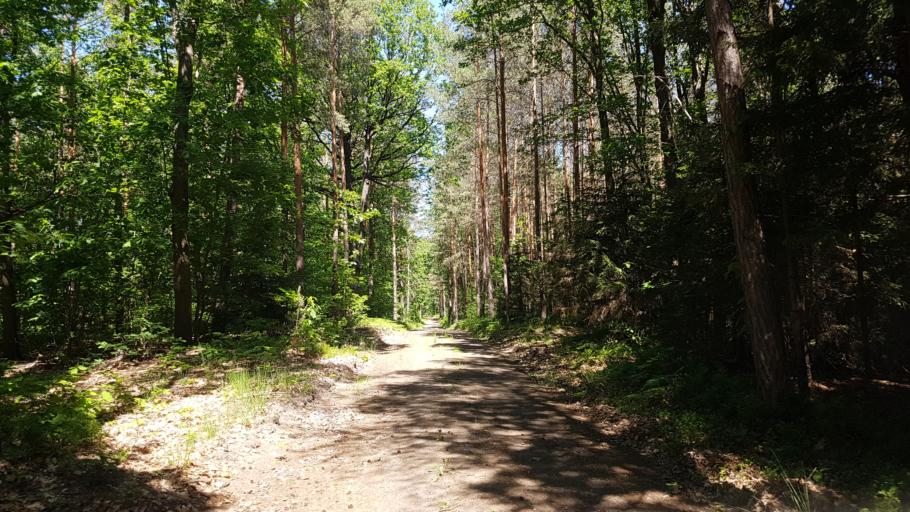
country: DE
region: Brandenburg
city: Hohenleipisch
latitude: 51.5327
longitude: 13.5772
